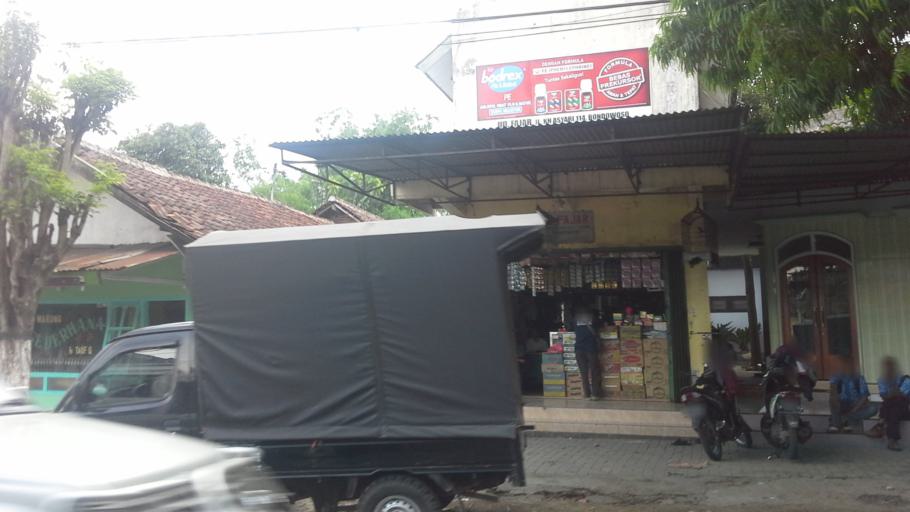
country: ID
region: East Java
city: Bondowoso
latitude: -7.9142
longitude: 113.8400
